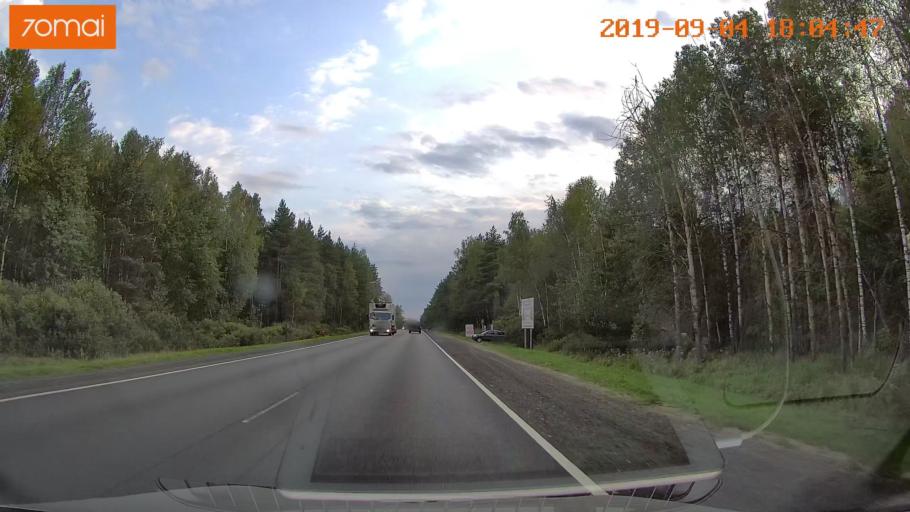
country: RU
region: Moskovskaya
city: Il'inskiy Pogost
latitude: 55.4484
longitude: 38.8347
